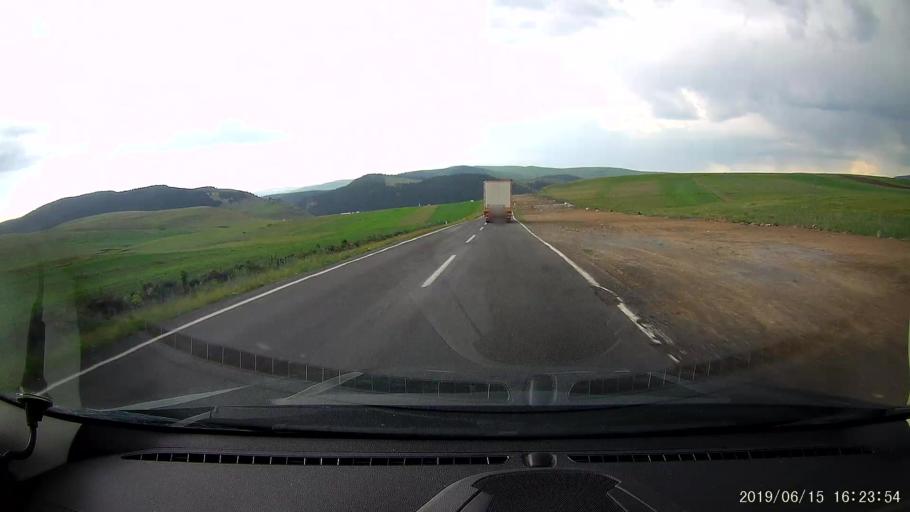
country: TR
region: Ardahan
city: Hanak
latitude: 41.1723
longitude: 42.8672
